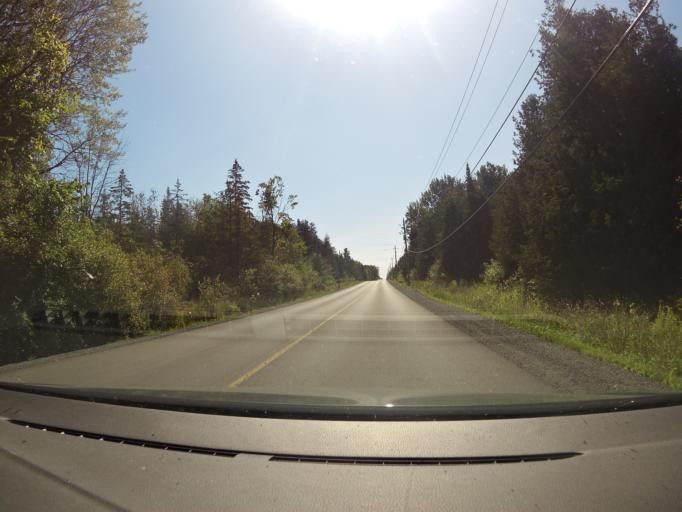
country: CA
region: Ontario
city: Carleton Place
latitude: 45.2698
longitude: -76.0339
